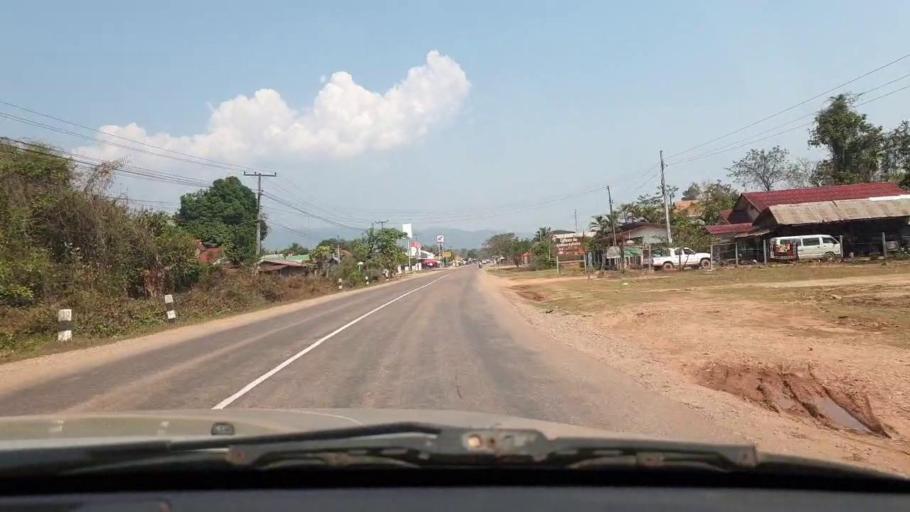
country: TH
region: Nong Khai
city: Rattanawapi
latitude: 18.1683
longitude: 103.0554
